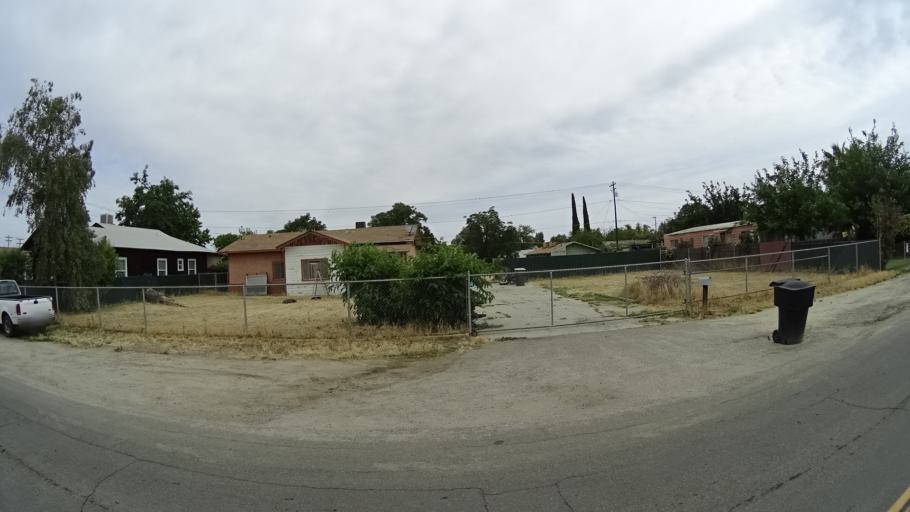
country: US
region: California
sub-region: Kings County
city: Hanford
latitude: 36.3240
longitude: -119.6618
